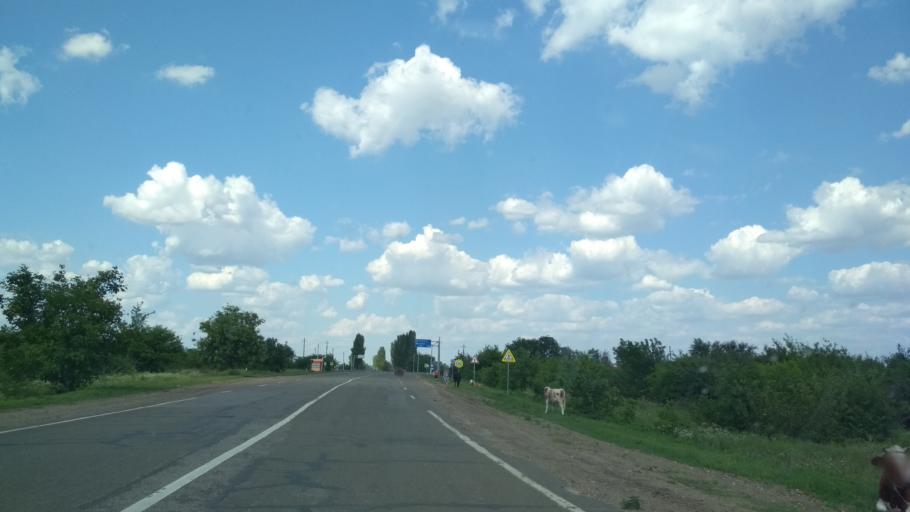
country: MD
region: Chisinau
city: Vadul lui Voda
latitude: 47.1174
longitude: 29.1086
